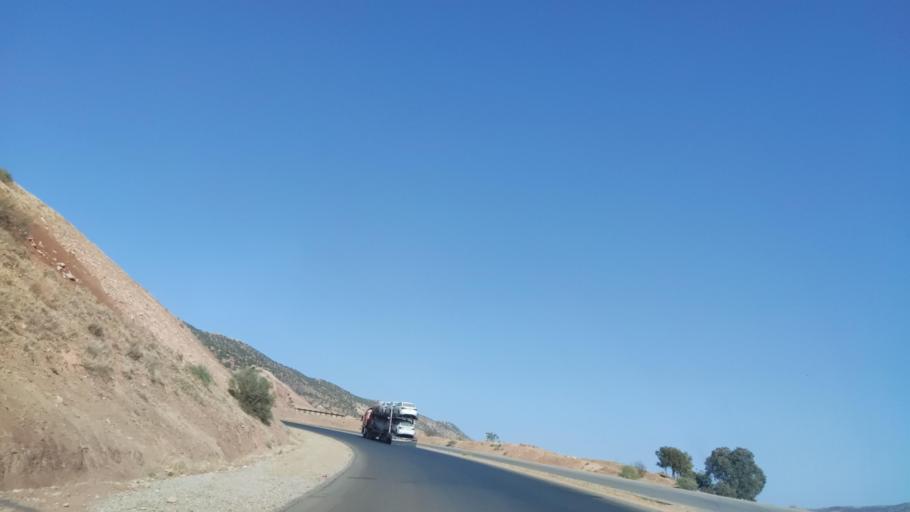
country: IQ
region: Arbil
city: Shaqlawah
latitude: 36.4326
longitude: 44.3111
